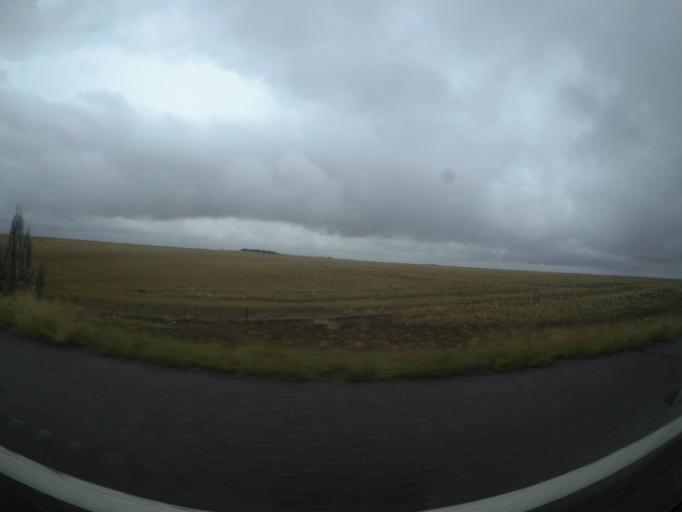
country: US
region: Colorado
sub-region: Arapahoe County
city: Byers
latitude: 39.7395
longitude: -104.1472
